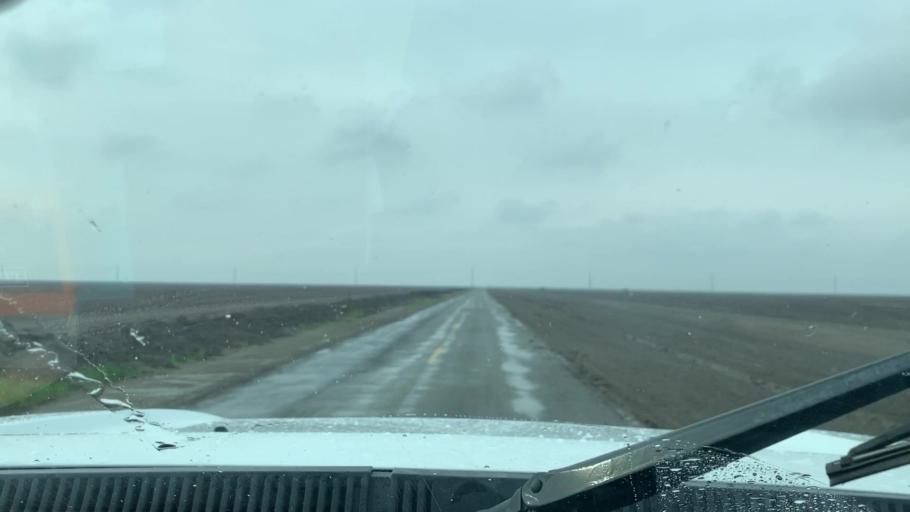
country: US
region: California
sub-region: Kings County
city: Corcoran
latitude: 36.0071
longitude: -119.5647
